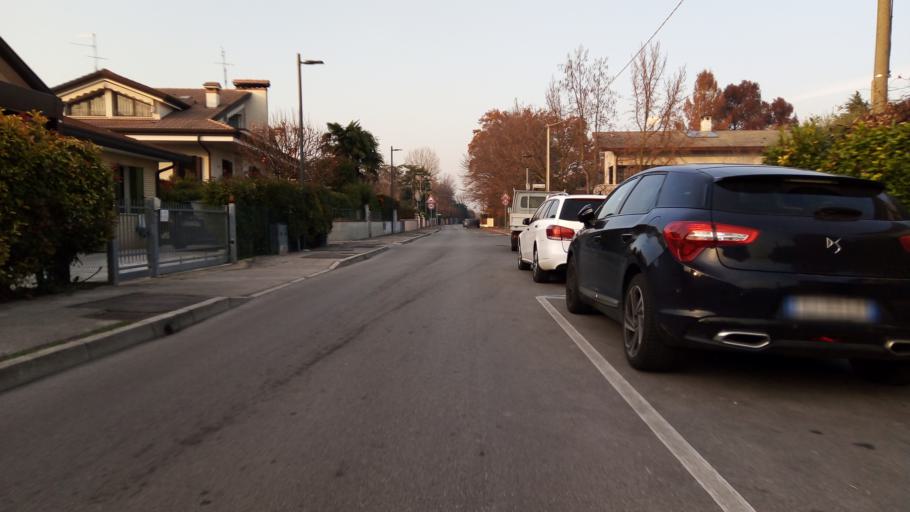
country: IT
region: Veneto
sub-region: Provincia di Padova
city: Abano Terme
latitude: 45.3559
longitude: 11.7717
